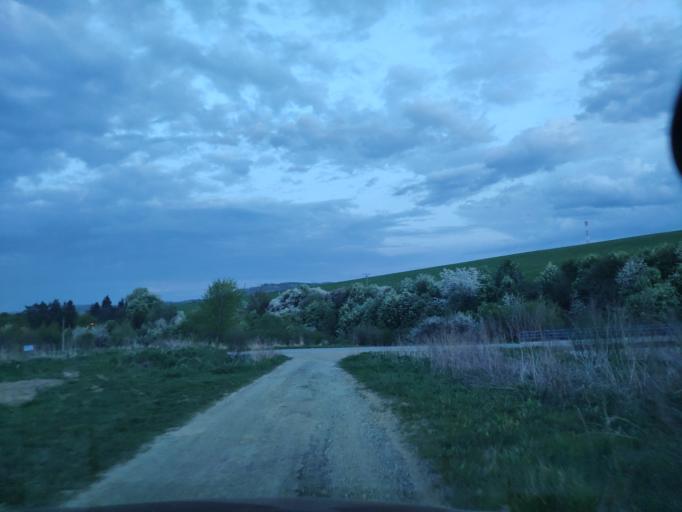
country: SK
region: Presovsky
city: Lipany
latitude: 49.1775
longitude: 20.8523
